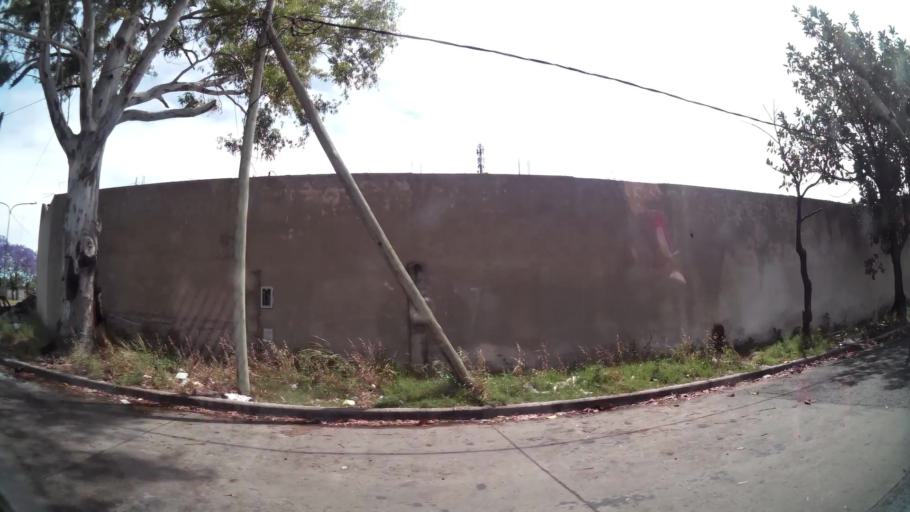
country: AR
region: Buenos Aires F.D.
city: Villa Lugano
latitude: -34.6681
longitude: -58.4331
